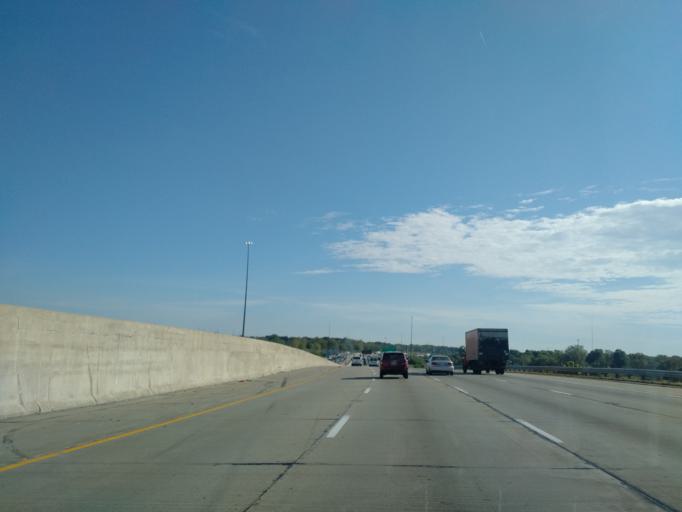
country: US
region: Indiana
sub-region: Marion County
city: Warren Park
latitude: 39.7978
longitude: -86.1006
